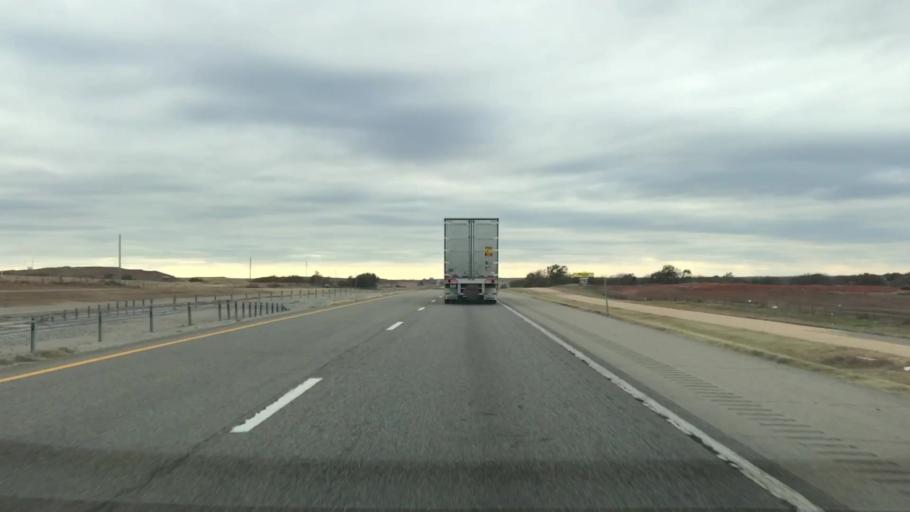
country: US
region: Oklahoma
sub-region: Washita County
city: Burns Flat
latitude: 35.4616
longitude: -99.1473
